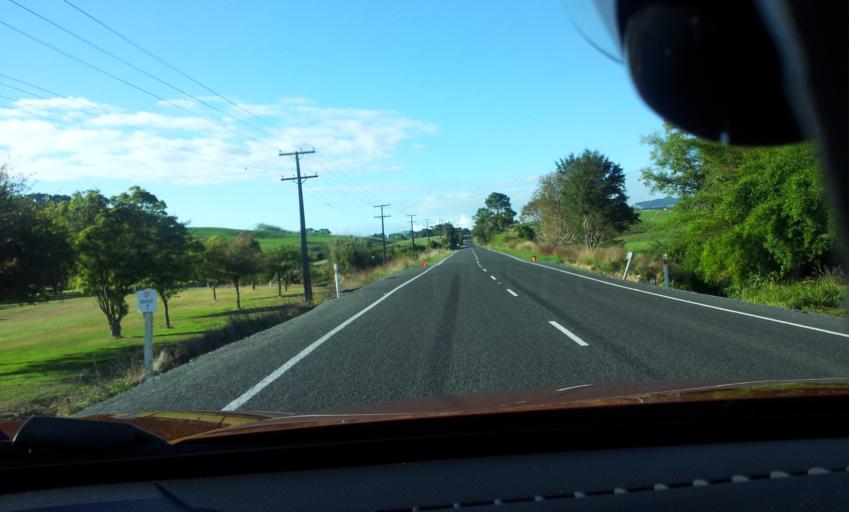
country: NZ
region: Waikato
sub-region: Hauraki District
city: Ngatea
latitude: -37.2970
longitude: 175.3752
